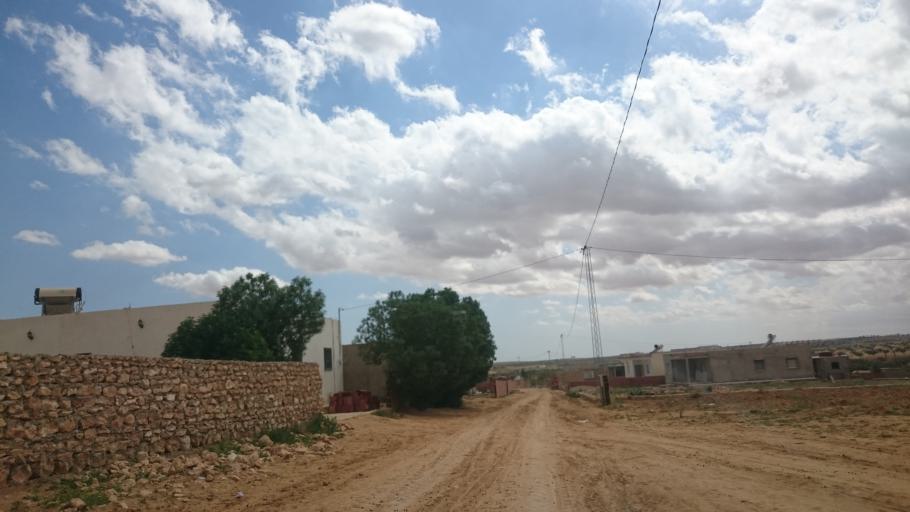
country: TN
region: Safaqis
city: Sfax
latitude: 34.7472
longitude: 10.4858
